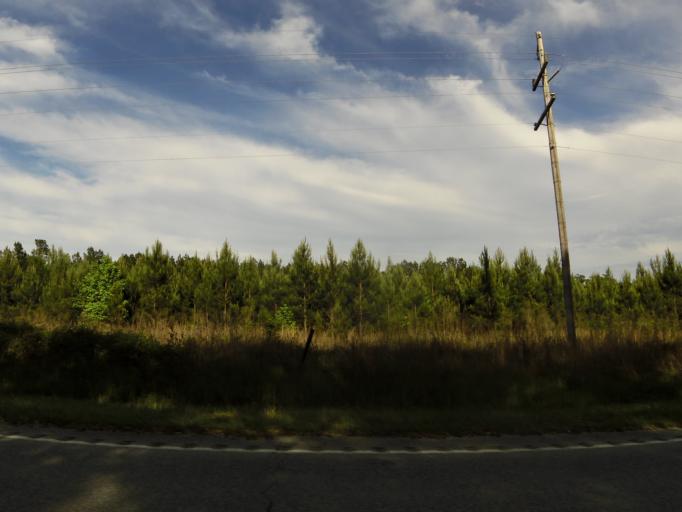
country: US
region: South Carolina
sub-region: Allendale County
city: Fairfax
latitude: 32.9125
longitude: -81.2376
